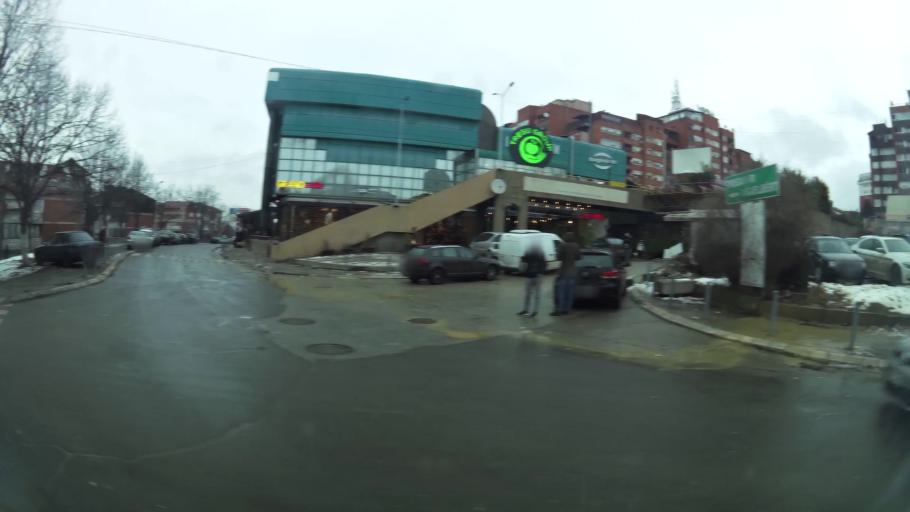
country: XK
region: Pristina
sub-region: Komuna e Prishtines
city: Pristina
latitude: 42.6501
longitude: 21.1674
